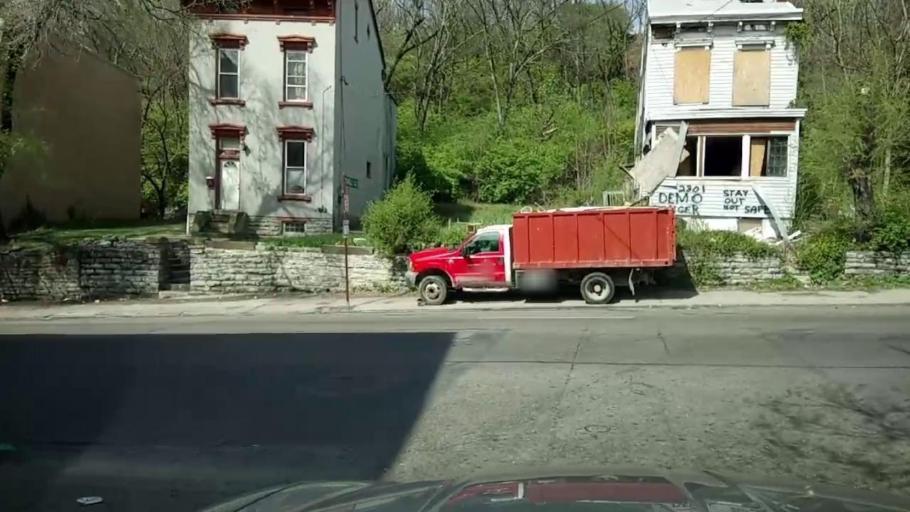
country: US
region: Kentucky
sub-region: Campbell County
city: Newport
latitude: 39.1234
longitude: -84.5143
